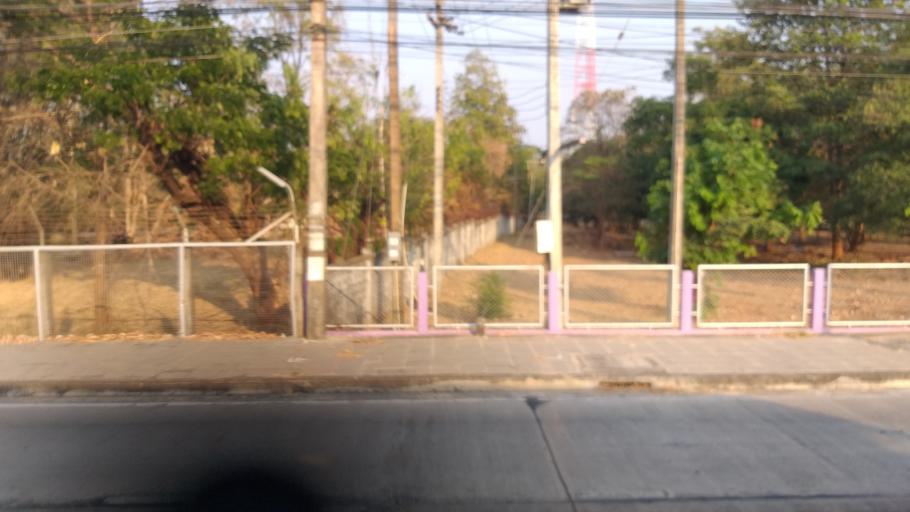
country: TH
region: Khon Kaen
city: Khon Kaen
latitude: 16.4766
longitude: 102.8330
